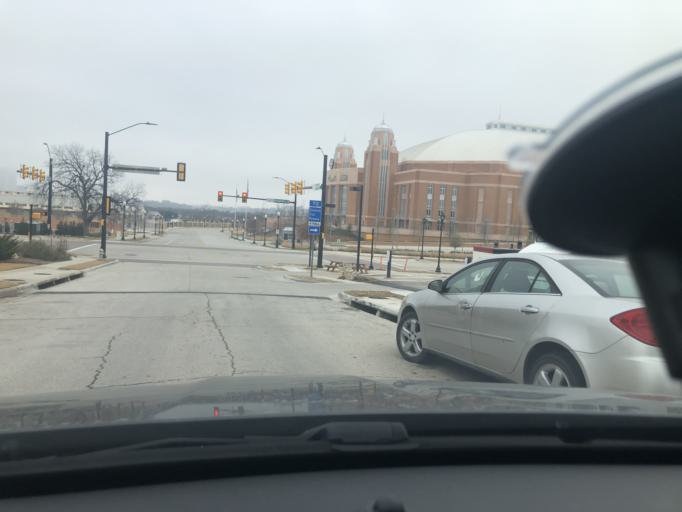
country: US
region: Texas
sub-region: Tarrant County
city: River Oaks
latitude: 32.7423
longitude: -97.3707
